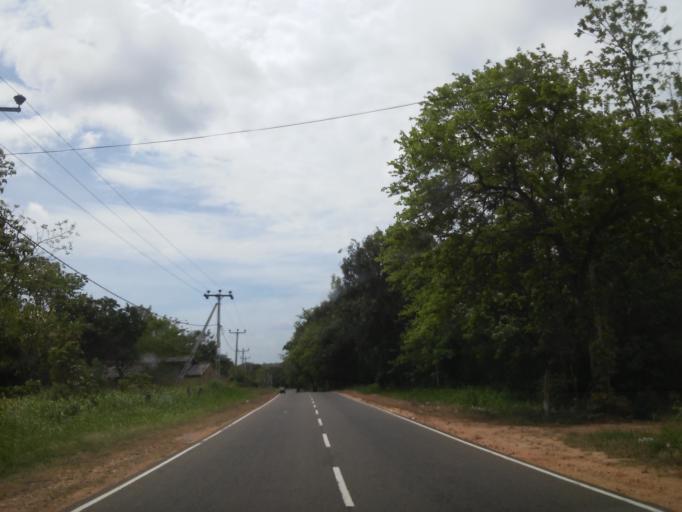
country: LK
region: Central
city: Sigiriya
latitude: 8.0445
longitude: 80.7335
